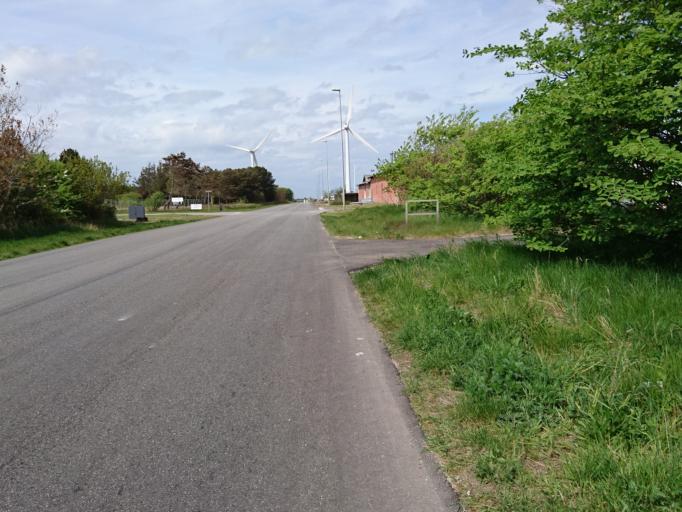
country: DK
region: North Denmark
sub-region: Frederikshavn Kommune
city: Skagen
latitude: 57.7329
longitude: 10.5685
